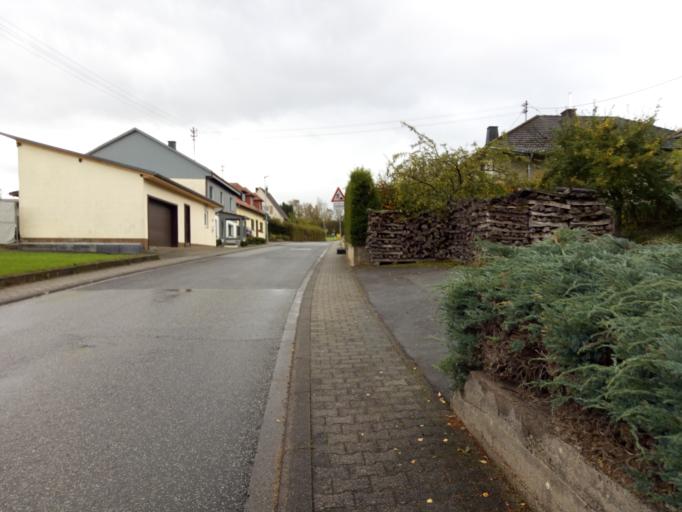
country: DE
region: Rheinland-Pfalz
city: Daubach
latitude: 49.8450
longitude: 7.6336
